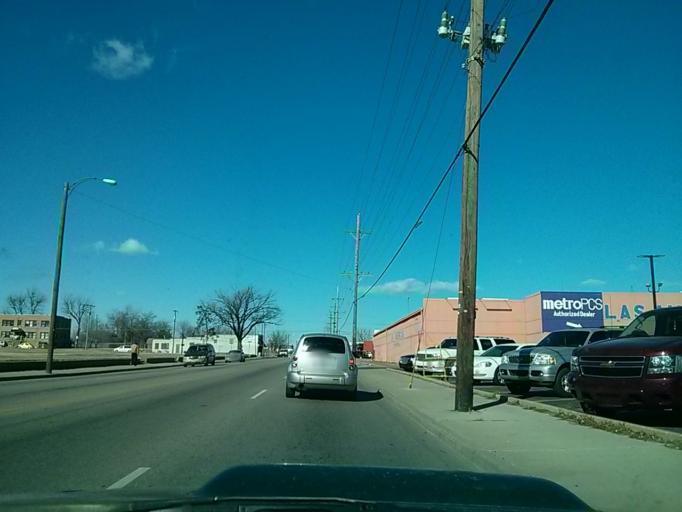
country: US
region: Oklahoma
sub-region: Tulsa County
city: Tulsa
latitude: 36.1613
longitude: -95.9581
